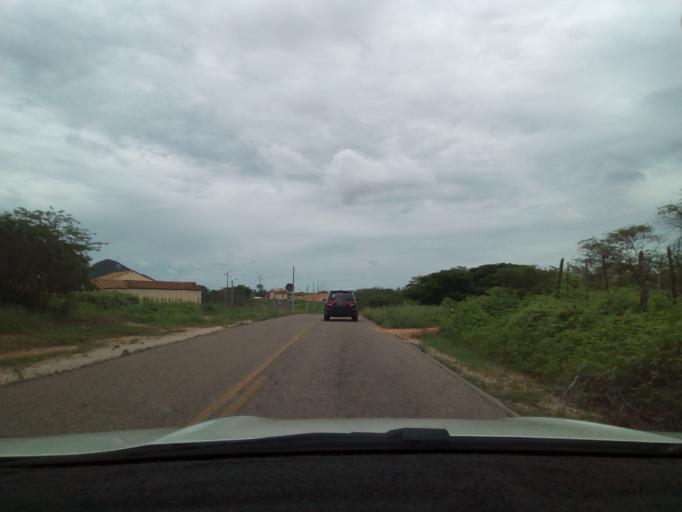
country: BR
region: Rio Grande do Norte
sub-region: Patu
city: Patu
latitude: -6.1136
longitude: -37.7341
